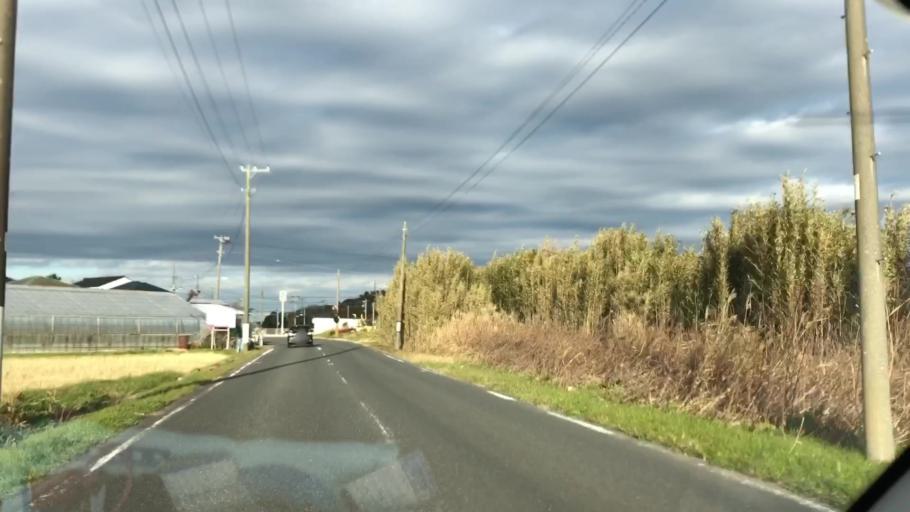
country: JP
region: Chiba
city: Tateyama
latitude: 35.0057
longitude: 139.8822
